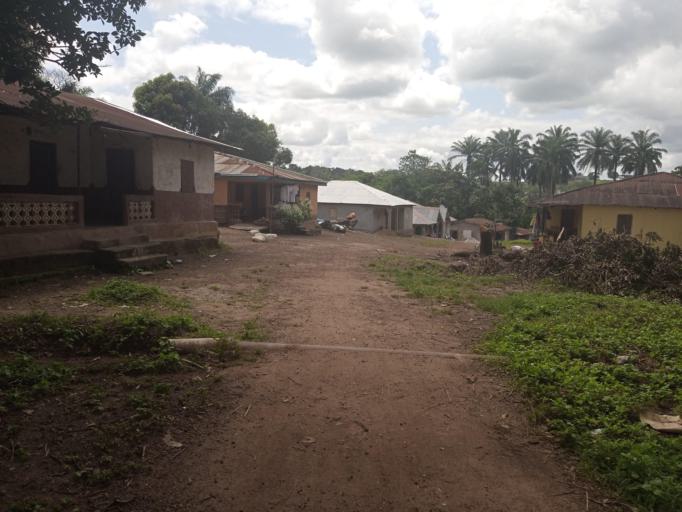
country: SL
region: Northern Province
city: Kamakwie
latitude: 9.4980
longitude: -12.2435
